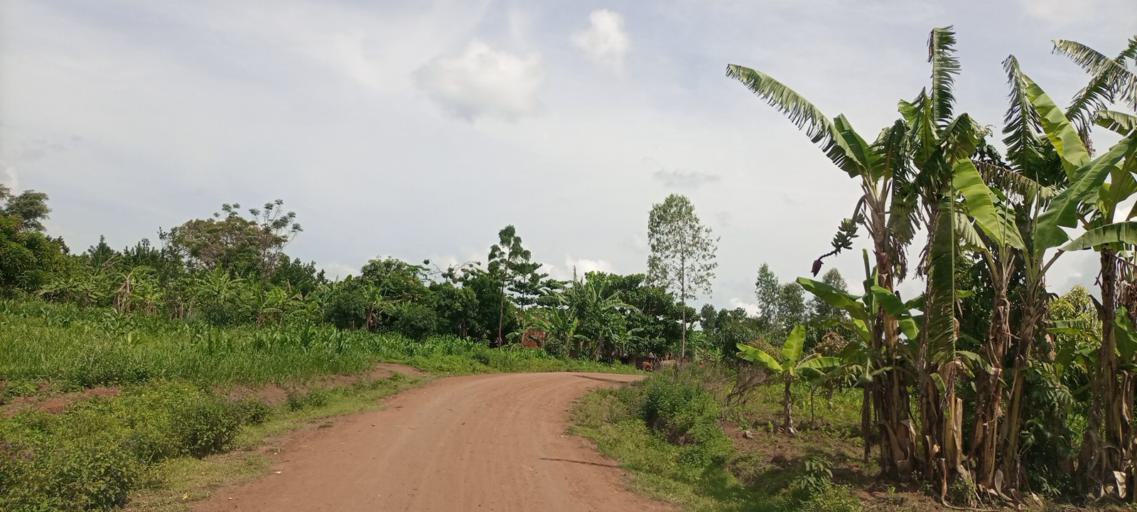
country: UG
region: Eastern Region
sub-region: Budaka District
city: Budaka
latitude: 1.1688
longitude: 33.9421
